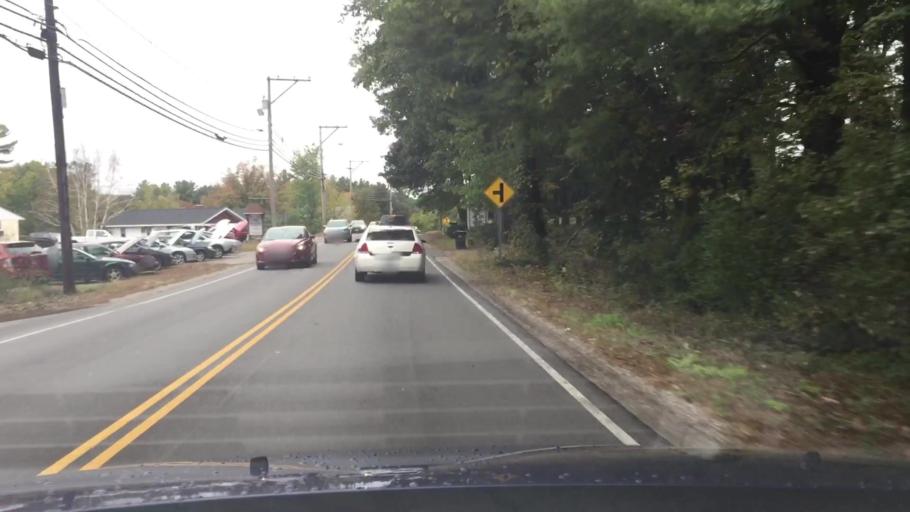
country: US
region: Massachusetts
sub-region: Middlesex County
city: Tyngsboro
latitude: 42.7170
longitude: -71.4158
